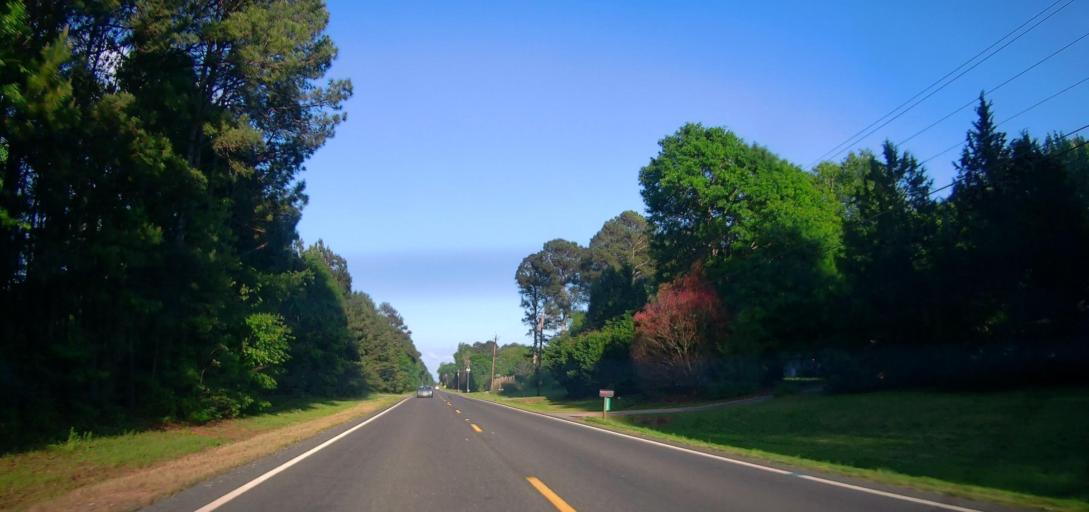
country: US
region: Georgia
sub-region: Walton County
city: Social Circle
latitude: 33.5094
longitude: -83.6772
